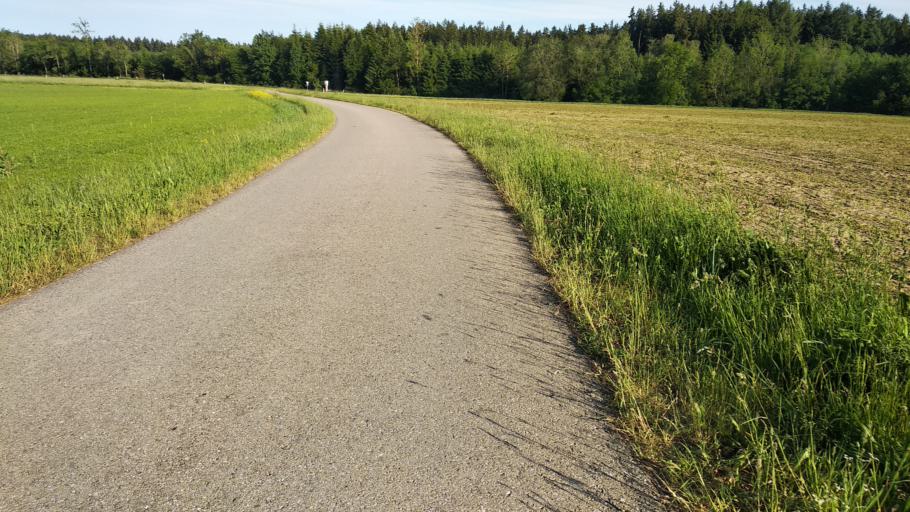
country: DE
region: Bavaria
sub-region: Swabia
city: Kronburg
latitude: 47.9039
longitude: 10.1422
